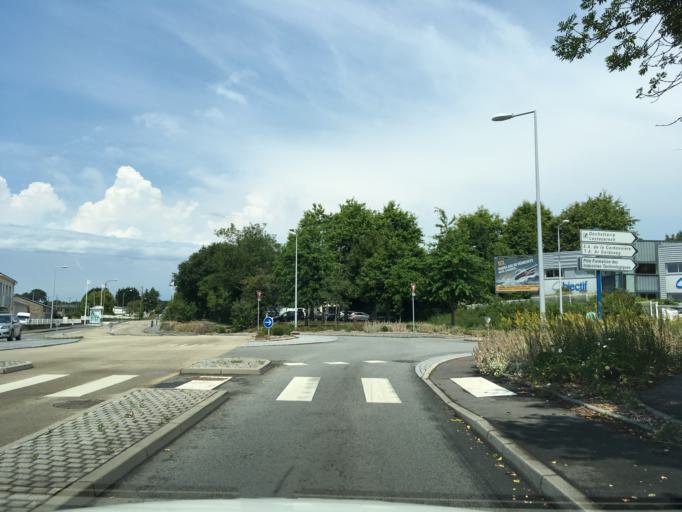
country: FR
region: Brittany
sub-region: Departement du Morbihan
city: Queven
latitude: 47.7713
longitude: -3.4041
